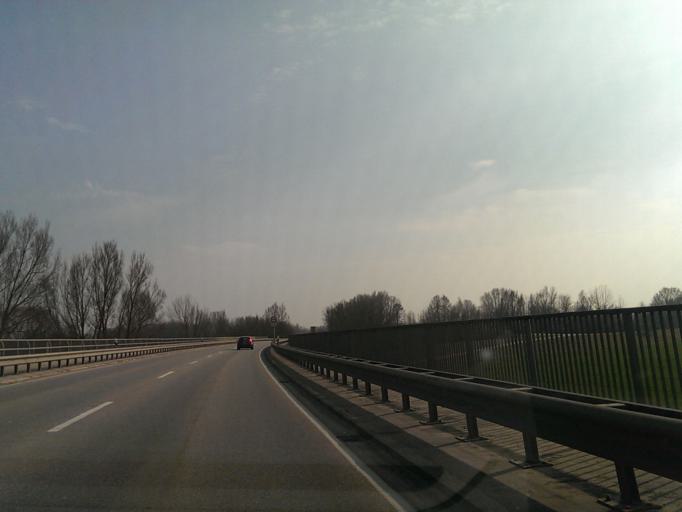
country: DE
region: Bavaria
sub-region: Upper Palatinate
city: Donaustauf
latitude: 49.0216
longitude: 12.2151
